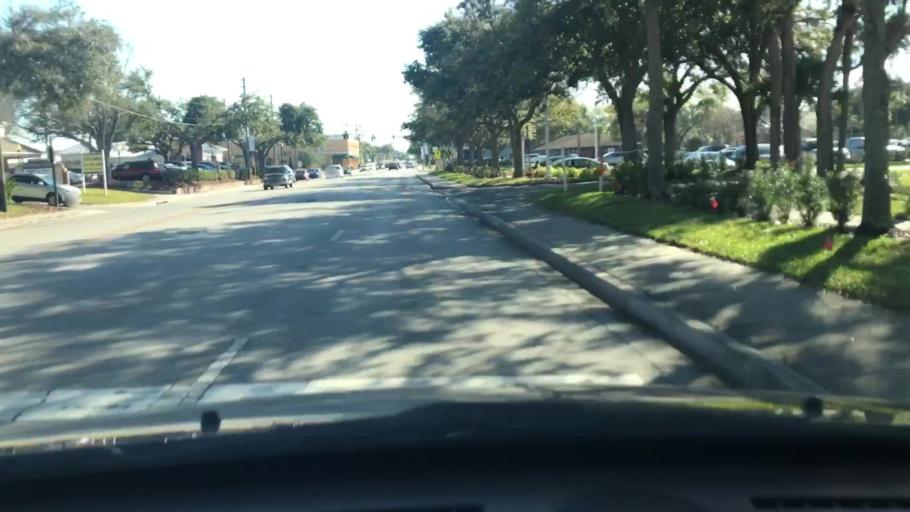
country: US
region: Florida
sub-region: Osceola County
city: Kissimmee
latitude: 28.3009
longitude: -81.4092
